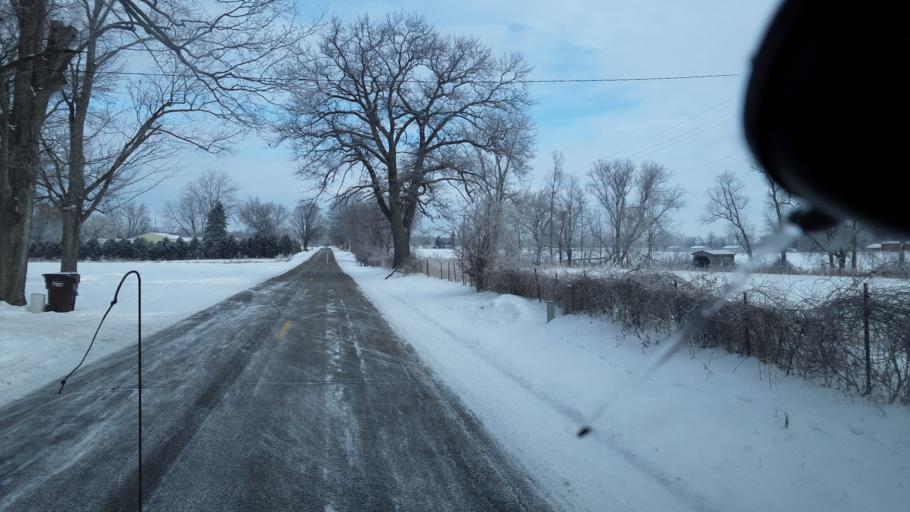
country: US
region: Michigan
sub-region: Ingham County
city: Leslie
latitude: 42.3817
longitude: -84.4924
